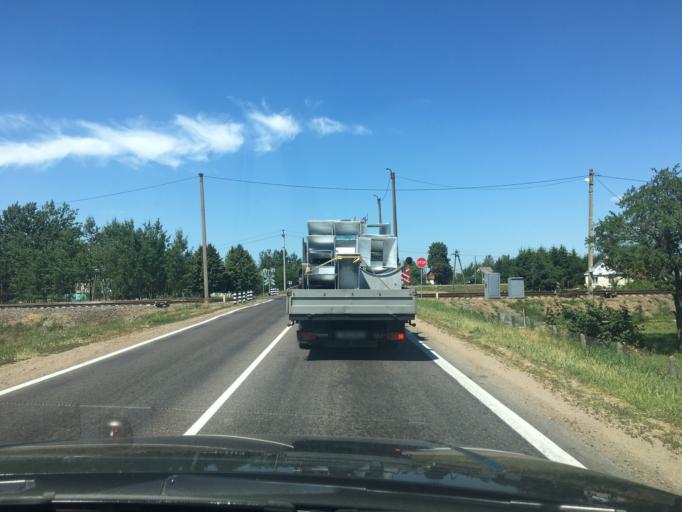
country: BY
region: Grodnenskaya
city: Iwye
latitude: 54.0607
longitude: 25.9117
